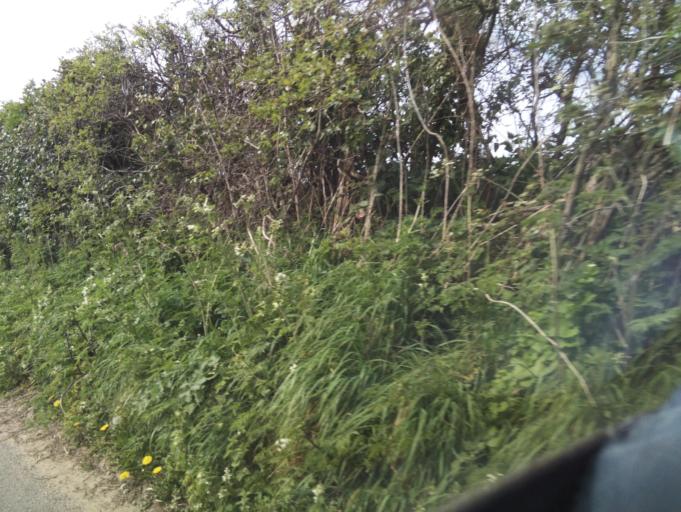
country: GB
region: England
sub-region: Dorset
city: Sherborne
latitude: 50.9683
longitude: -2.5032
